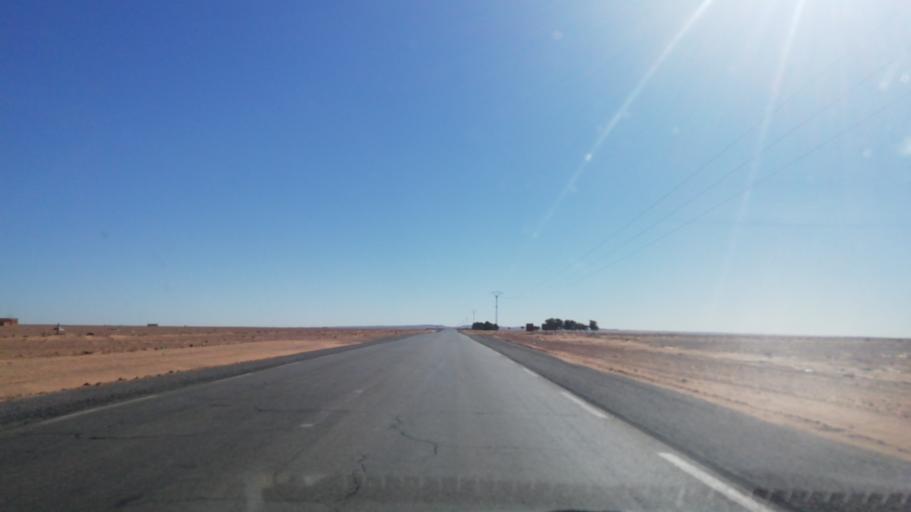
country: DZ
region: Saida
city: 'Ain el Hadjar
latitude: 34.0128
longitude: 0.1149
